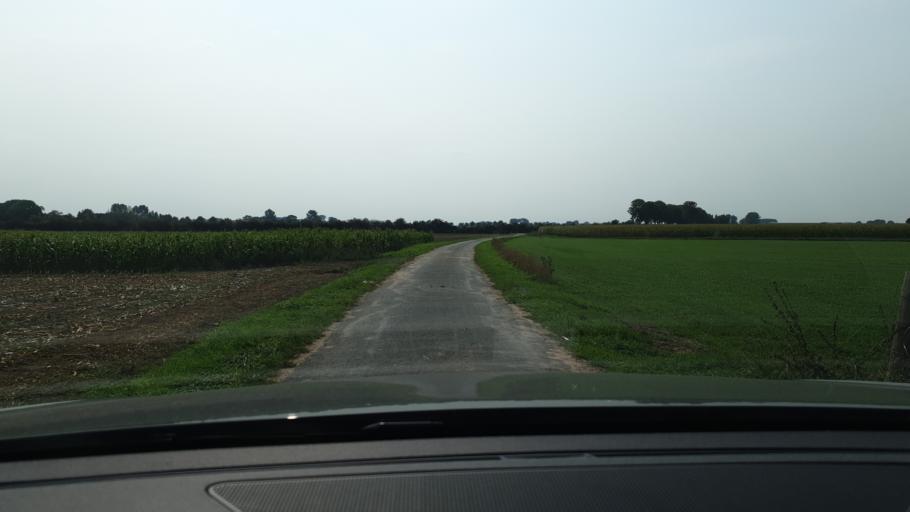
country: NL
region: Gelderland
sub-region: Gemeente Zevenaar
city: Zevenaar
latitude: 51.8552
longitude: 6.0595
